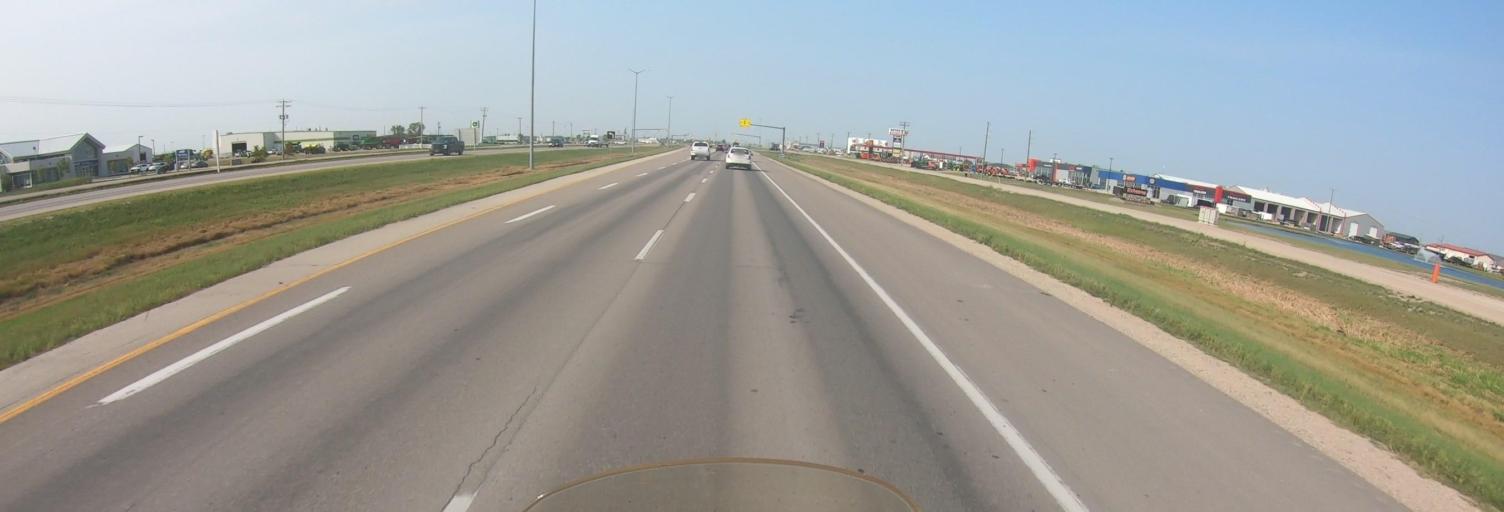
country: CA
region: Manitoba
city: Steinbach
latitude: 49.5565
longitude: -96.6878
